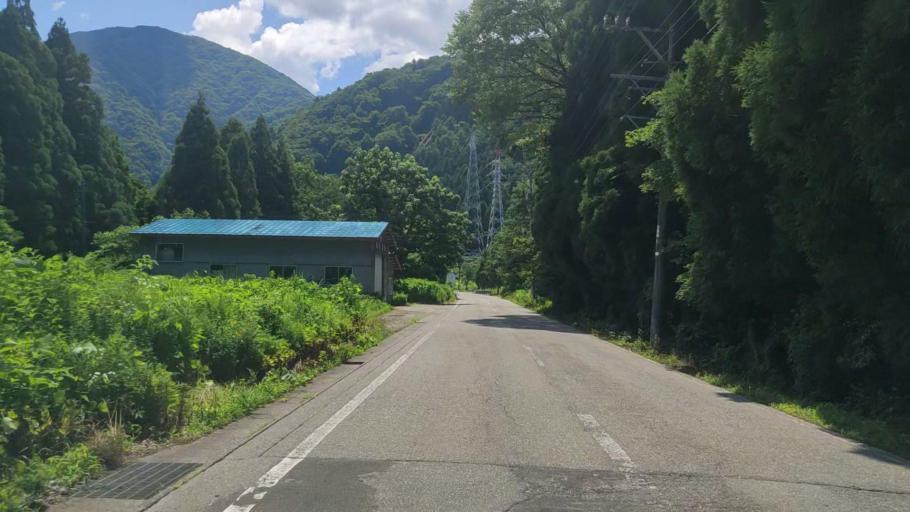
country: JP
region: Fukui
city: Ono
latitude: 35.9373
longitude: 136.5525
